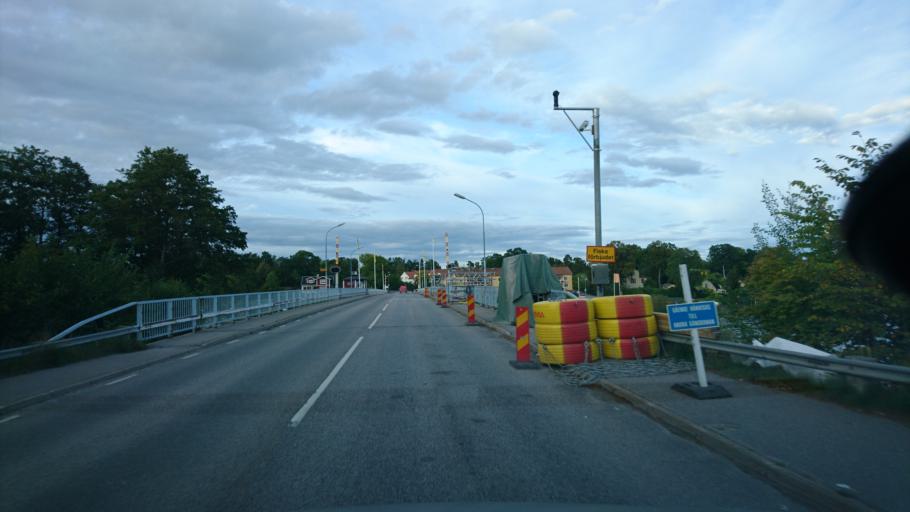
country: SE
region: Soedermanland
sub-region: Strangnas Kommun
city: Stallarholmen
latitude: 59.3639
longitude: 17.2057
